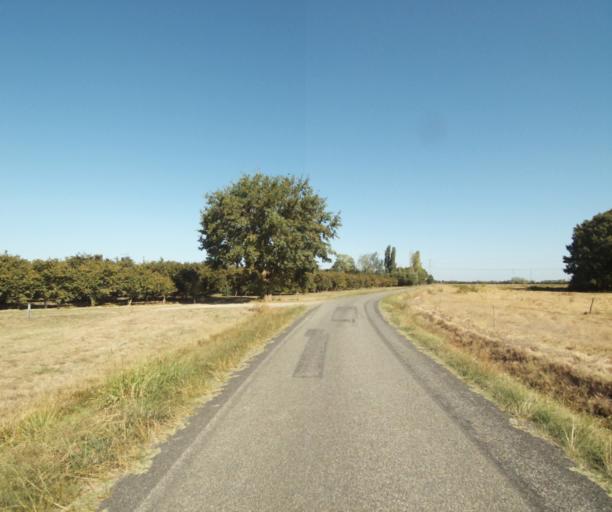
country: FR
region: Midi-Pyrenees
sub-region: Departement du Tarn-et-Garonne
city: Verdun-sur-Garonne
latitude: 43.8279
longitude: 1.2261
